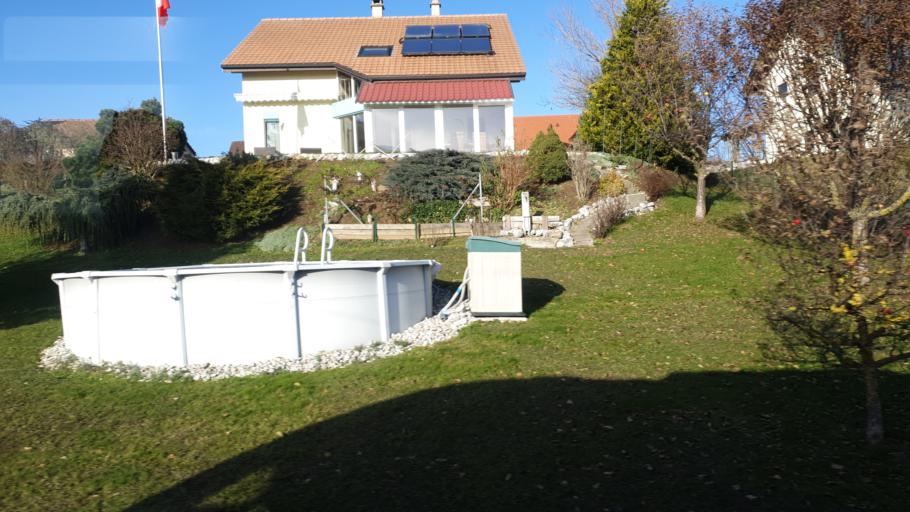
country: CH
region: Fribourg
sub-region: Gruyere District
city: Sales
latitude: 46.6189
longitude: 6.9868
